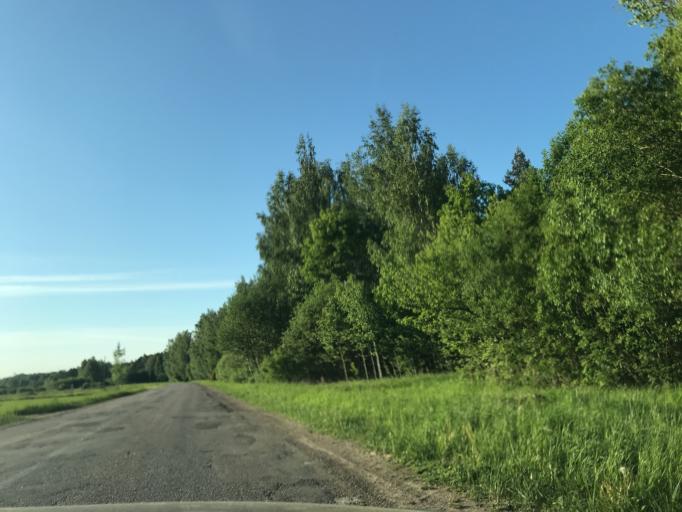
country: LV
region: Ozolnieku
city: Ozolnieki
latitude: 56.5943
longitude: 23.8043
